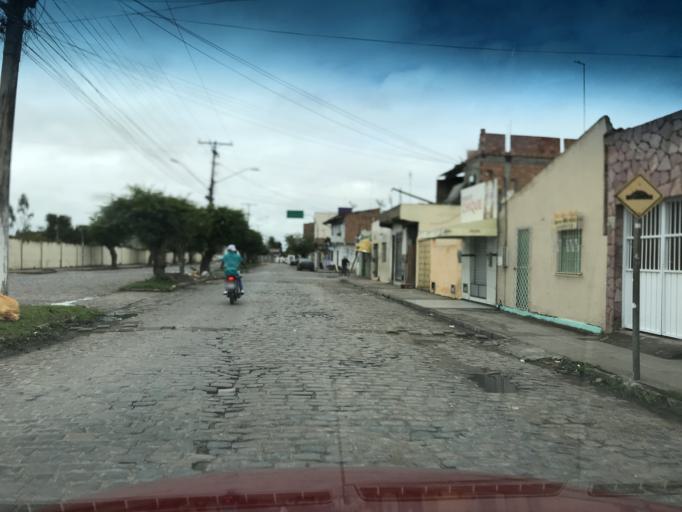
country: BR
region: Bahia
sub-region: Cruz Das Almas
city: Cruz das Almas
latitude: -12.6627
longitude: -39.1007
